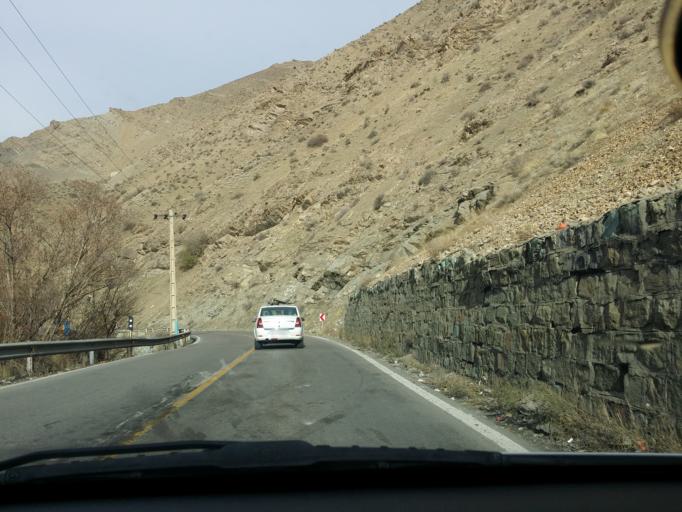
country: IR
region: Tehran
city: Tajrish
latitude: 36.0305
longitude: 51.2352
